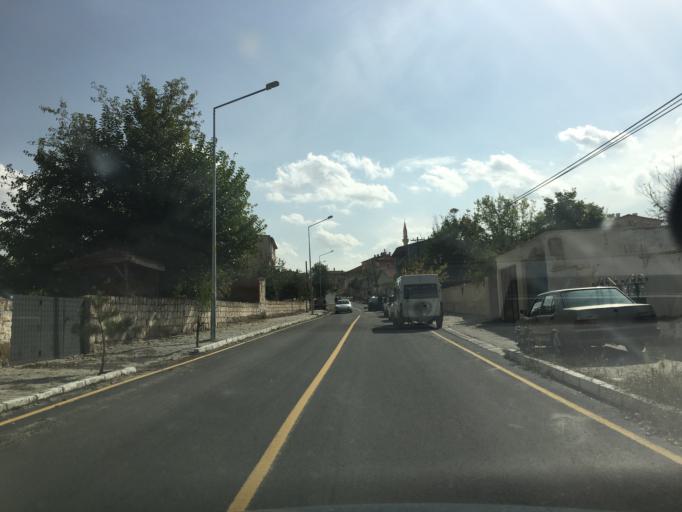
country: TR
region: Nevsehir
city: Goereme
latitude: 38.6723
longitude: 34.8399
